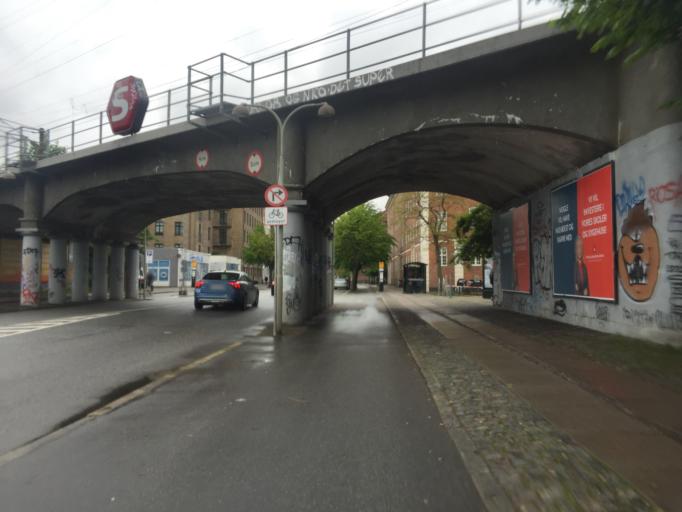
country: DK
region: Capital Region
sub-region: Frederiksberg Kommune
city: Frederiksberg
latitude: 55.6956
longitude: 12.5274
